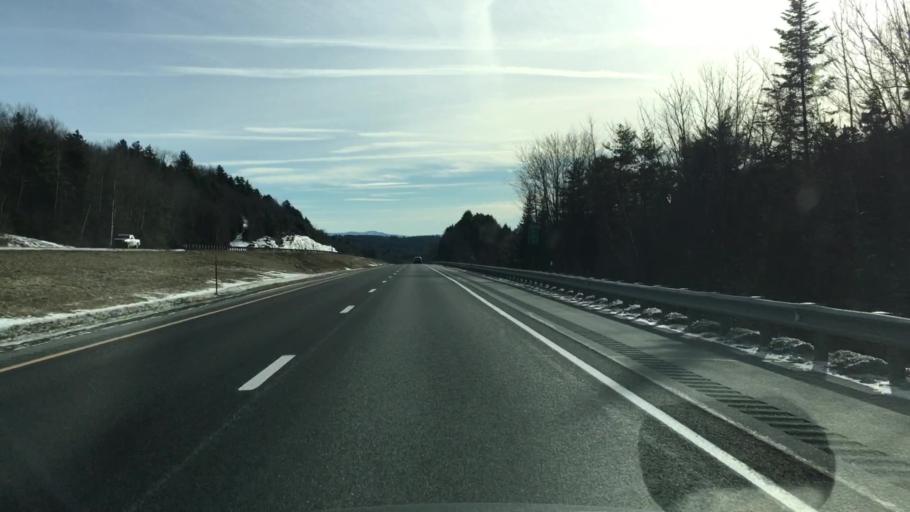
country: US
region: New Hampshire
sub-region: Sullivan County
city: Grantham
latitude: 43.5524
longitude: -72.1409
